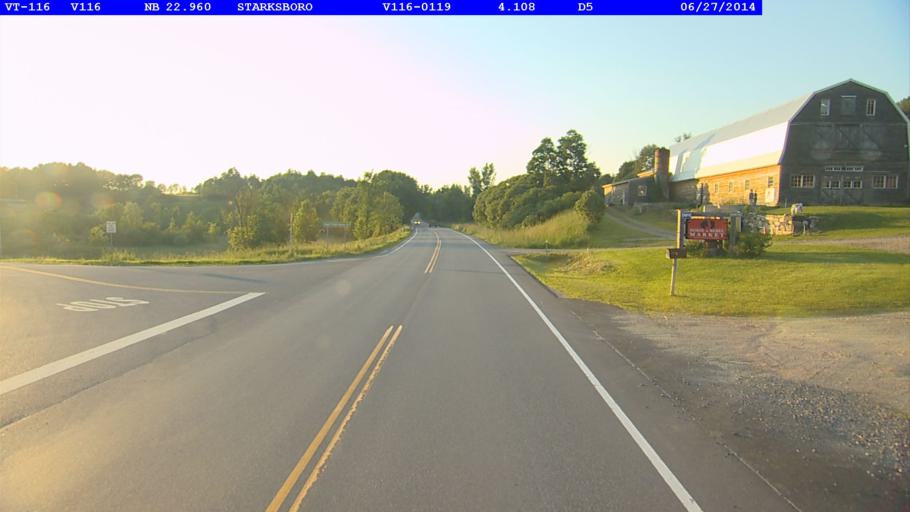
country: US
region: Vermont
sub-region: Chittenden County
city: Hinesburg
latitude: 44.2438
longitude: -73.0589
